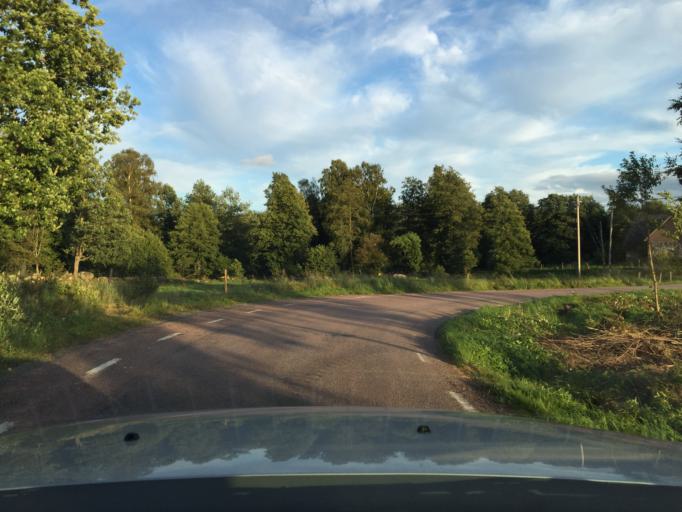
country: SE
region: Skane
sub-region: Hassleholms Kommun
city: Tormestorp
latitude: 56.0073
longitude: 13.7871
